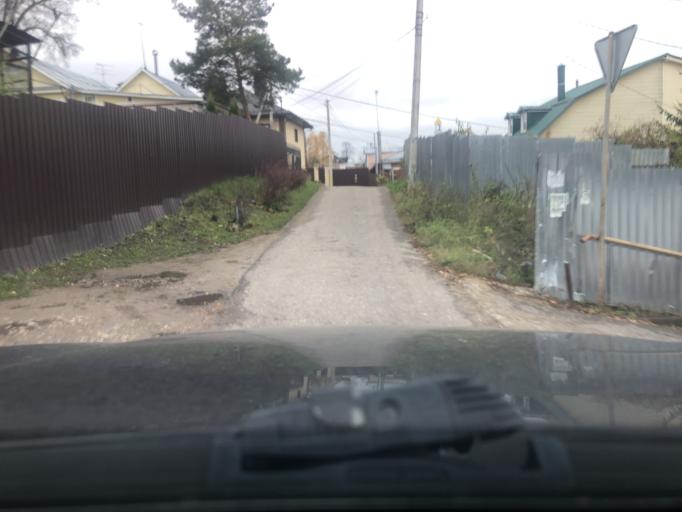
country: RU
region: Moskovskaya
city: Sergiyev Posad
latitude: 56.3173
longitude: 38.1294
